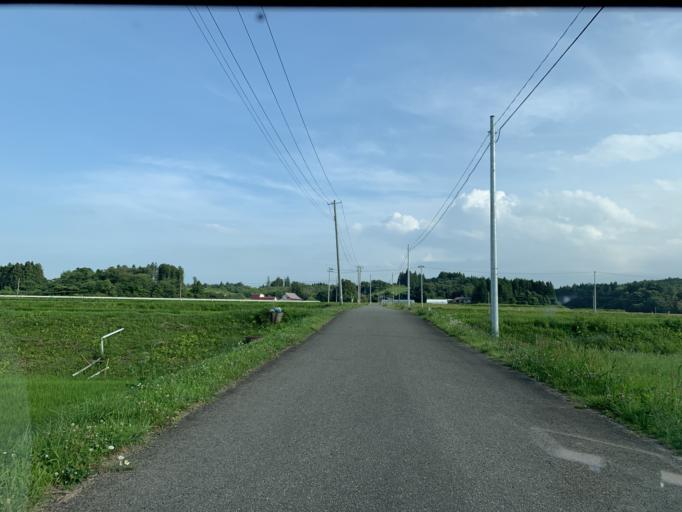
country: JP
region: Iwate
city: Ichinoseki
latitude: 38.8402
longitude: 141.1356
